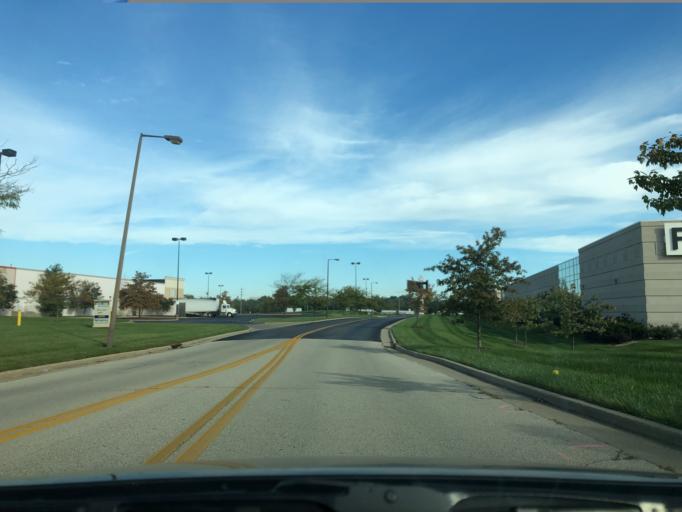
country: US
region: Ohio
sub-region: Hamilton County
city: Glendale
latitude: 39.2904
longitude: -84.4534
